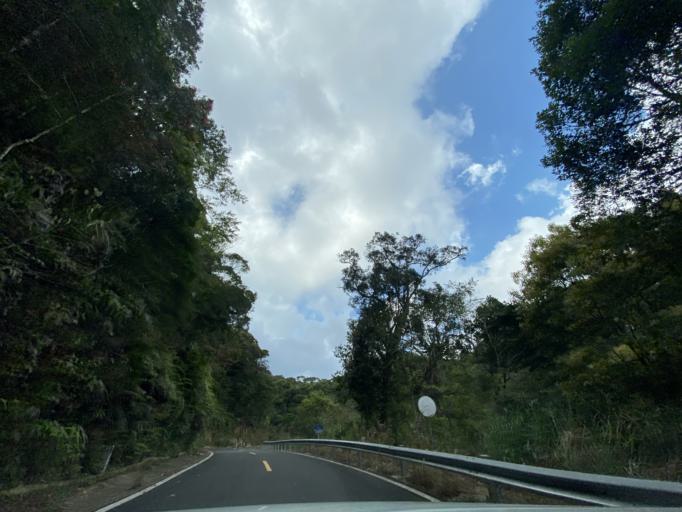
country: CN
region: Hainan
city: Diaoluoshan
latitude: 18.7216
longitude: 109.8743
